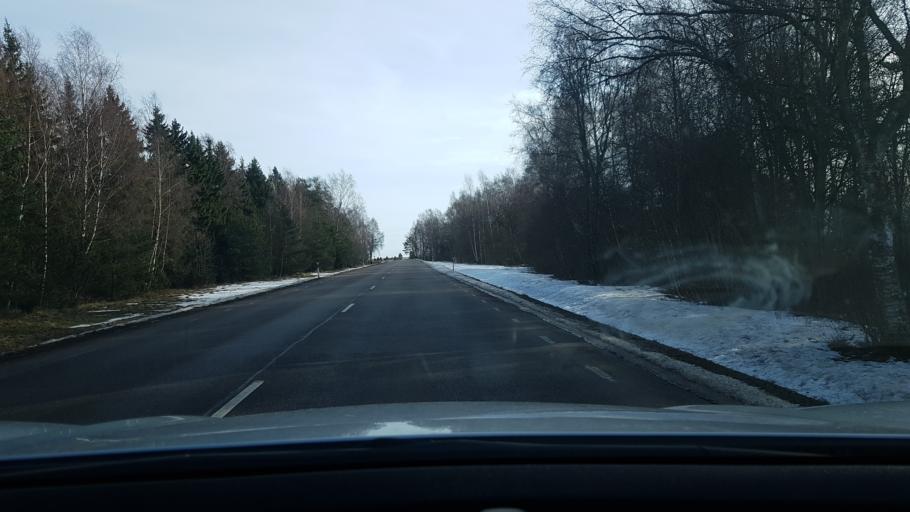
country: EE
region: Saare
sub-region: Orissaare vald
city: Orissaare
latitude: 58.5497
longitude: 23.1194
